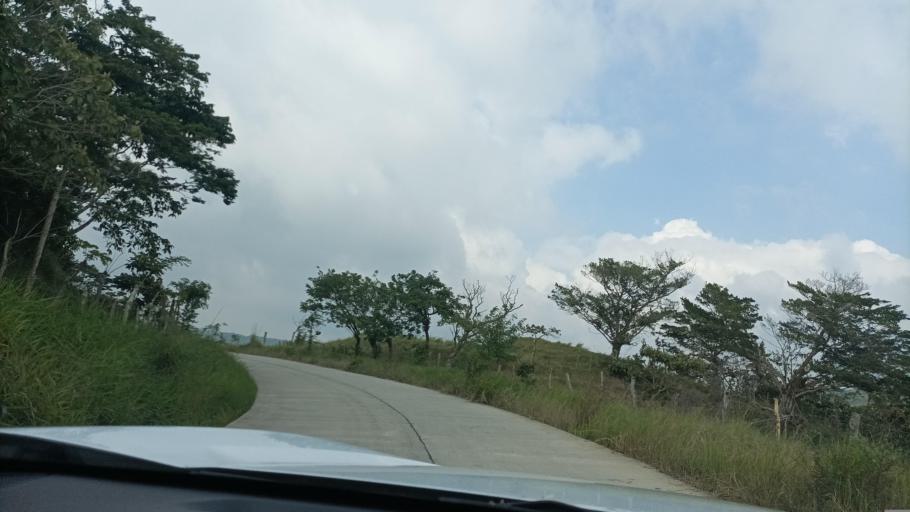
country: MX
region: Veracruz
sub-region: Moloacan
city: Tlacuilolapan
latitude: 18.0793
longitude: -94.2854
